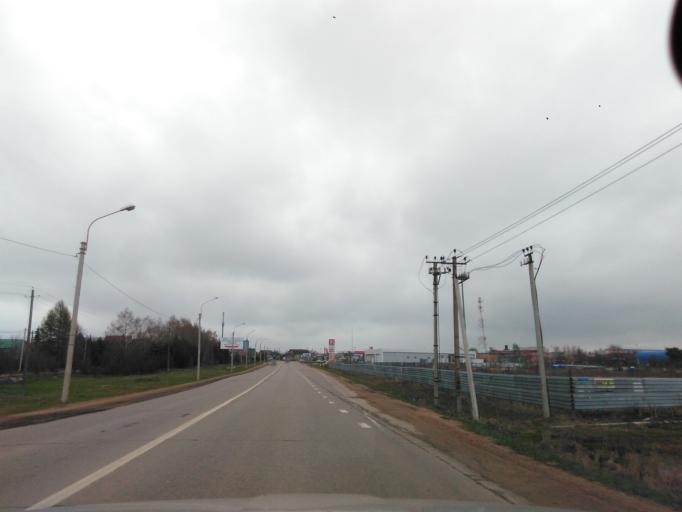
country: RU
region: Moskovskaya
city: Pavlovskaya Sloboda
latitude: 55.8172
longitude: 37.0683
